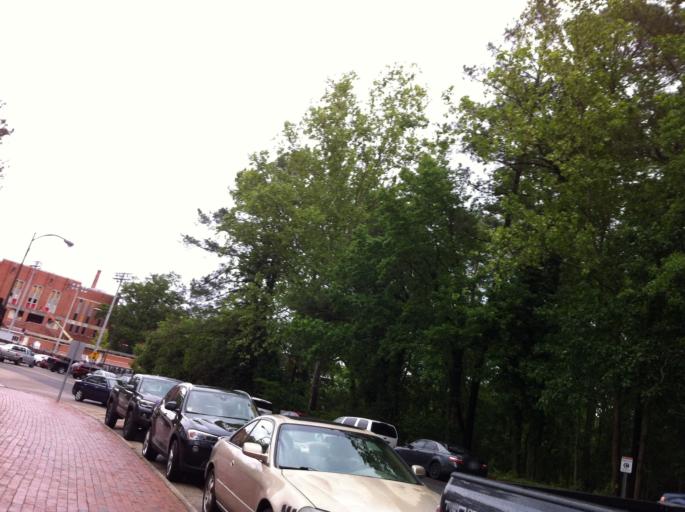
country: US
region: North Carolina
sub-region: Wake County
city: West Raleigh
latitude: 35.7818
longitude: -78.6718
